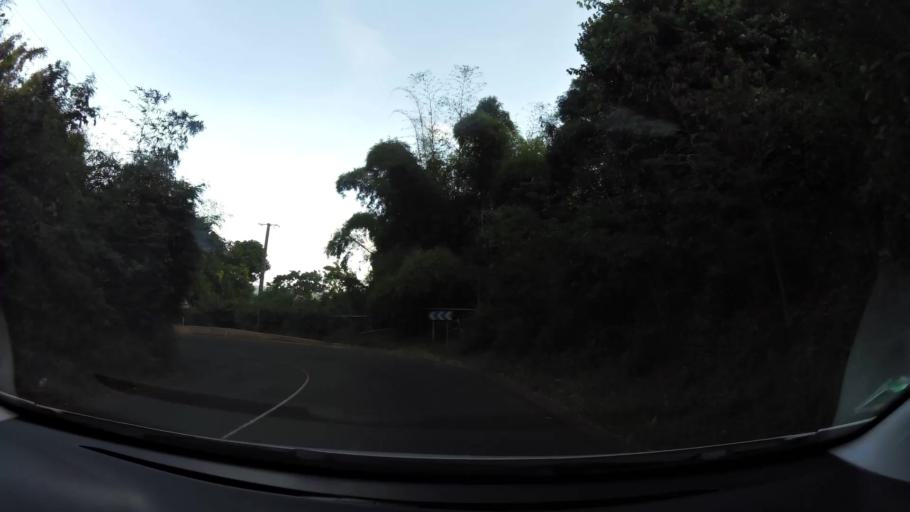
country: YT
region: Dembeni
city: Dembeni
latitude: -12.8220
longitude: 45.1937
